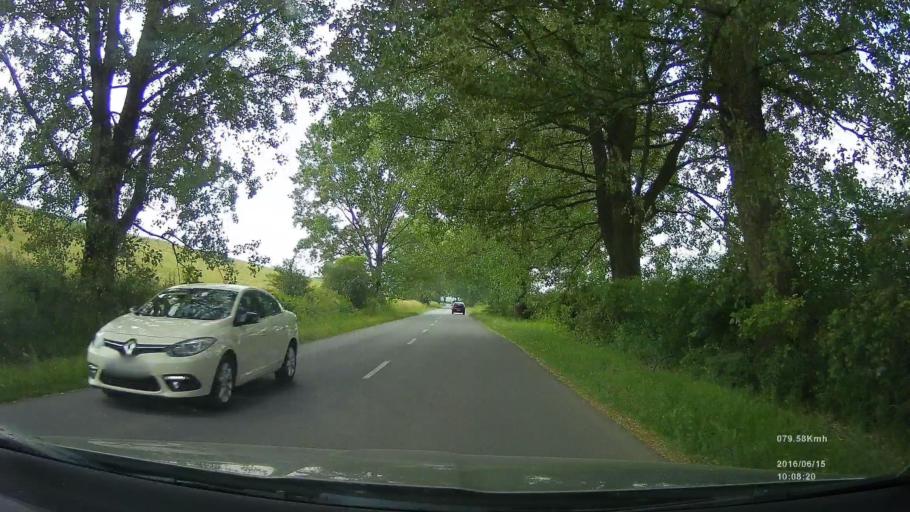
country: SK
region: Kosicky
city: Kosice
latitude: 48.7683
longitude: 21.3308
